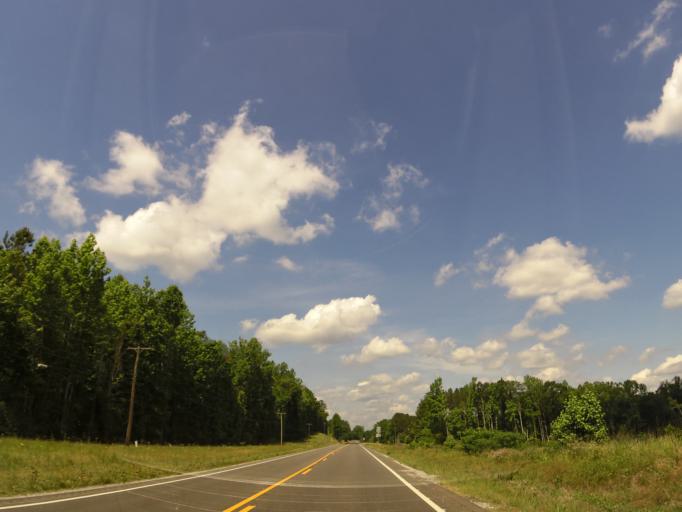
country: US
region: Alabama
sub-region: Marion County
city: Guin
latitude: 33.9546
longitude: -87.9515
